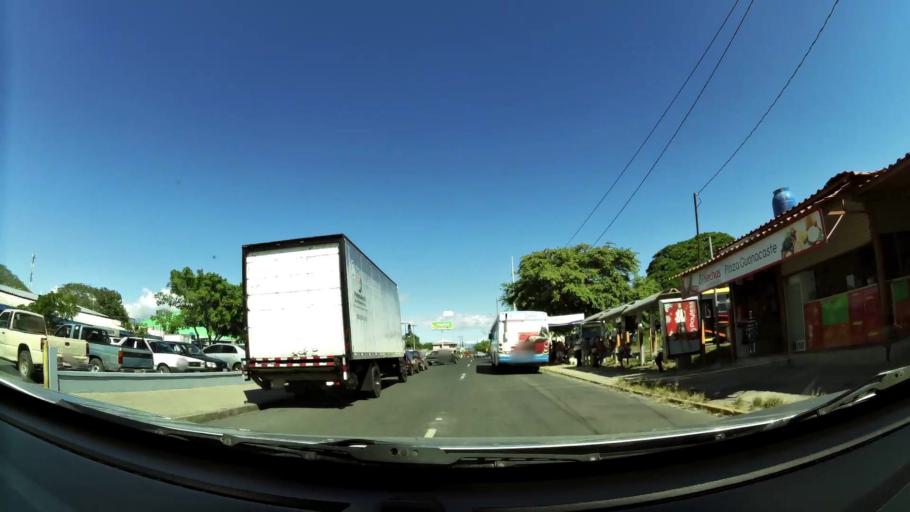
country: CR
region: Guanacaste
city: Liberia
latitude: 10.6305
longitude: -85.4436
